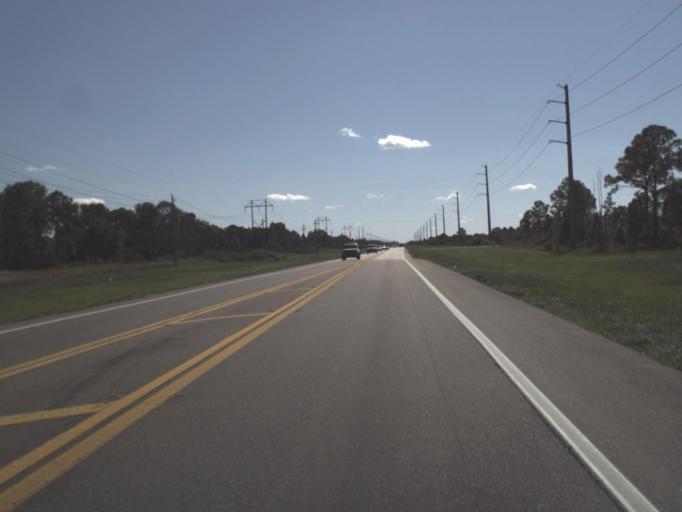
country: US
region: Florida
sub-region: Lee County
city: Gateway
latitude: 26.5748
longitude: -81.6978
